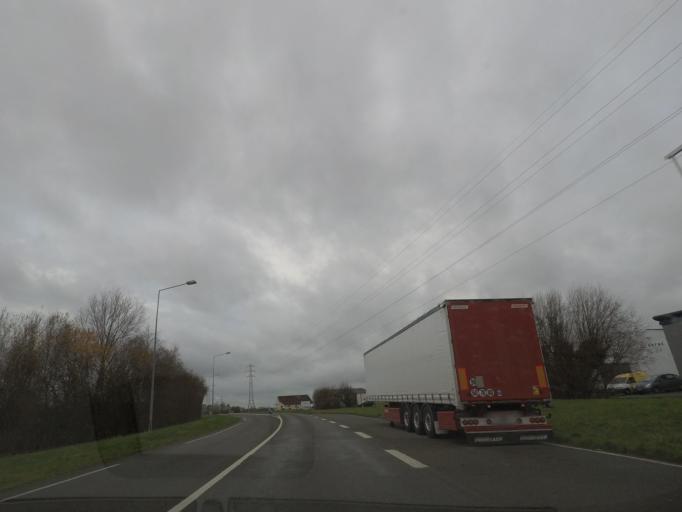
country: FR
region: Pays de la Loire
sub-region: Departement de la Sarthe
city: La Ferte-Bernard
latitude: 48.1923
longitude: 0.6285
